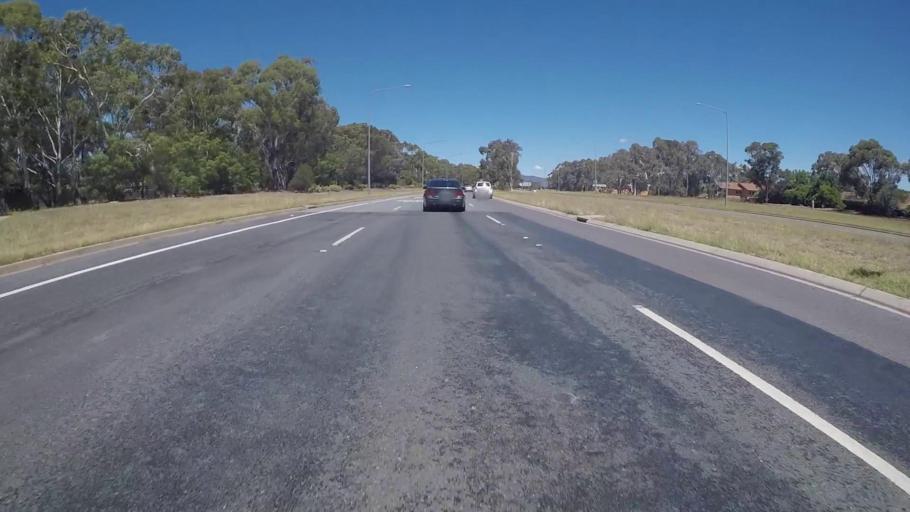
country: AU
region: Australian Capital Territory
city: Macarthur
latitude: -35.4033
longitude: 149.0748
